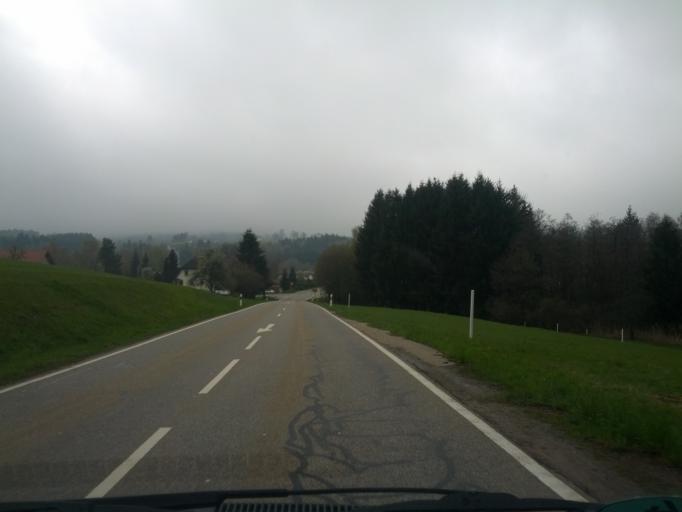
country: DE
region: Baden-Wuerttemberg
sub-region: Freiburg Region
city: Rickenbach
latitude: 47.6205
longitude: 8.0138
